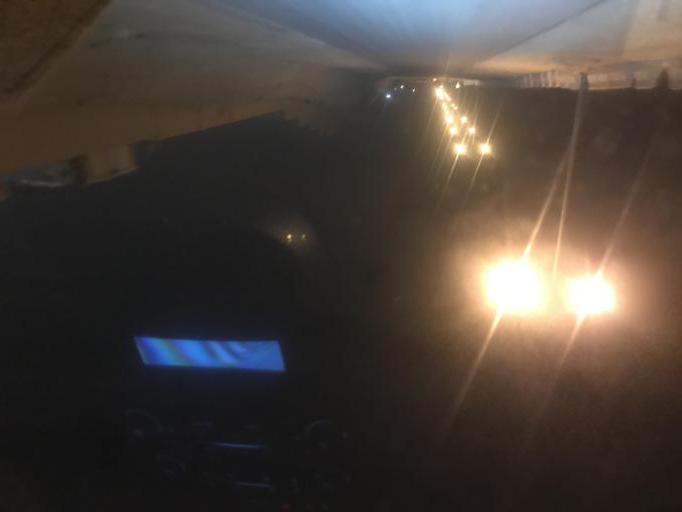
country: SA
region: Ar Riyad
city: Riyadh
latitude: 24.7577
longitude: 46.5901
